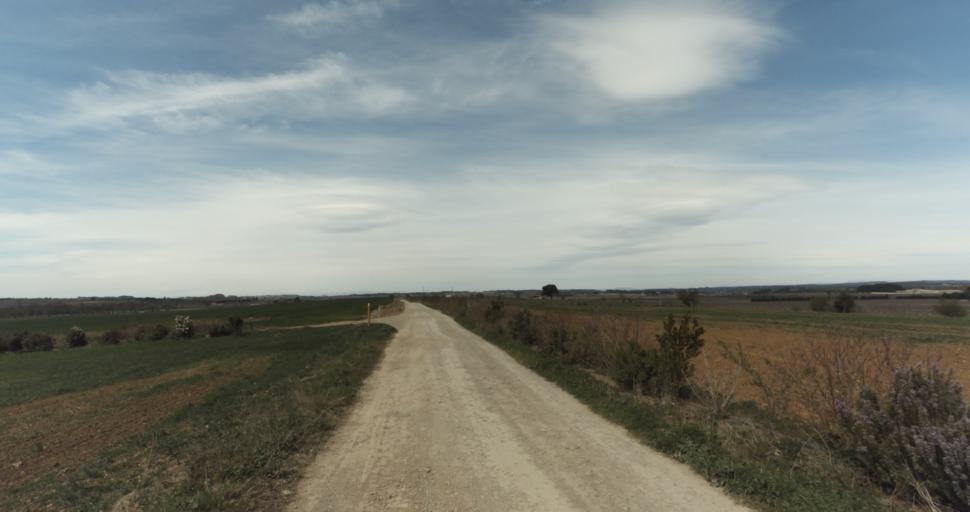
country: FR
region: Languedoc-Roussillon
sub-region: Departement de l'Herault
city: Meze
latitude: 43.4007
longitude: 3.5610
